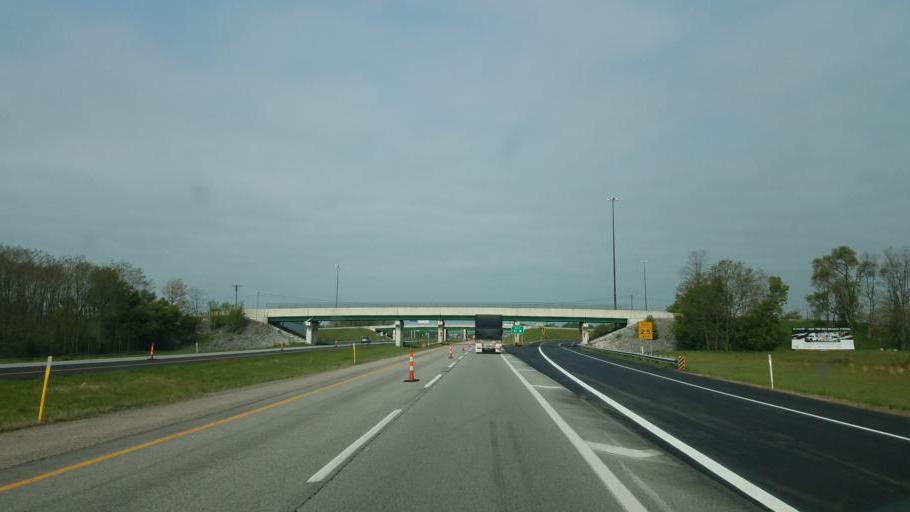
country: US
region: Indiana
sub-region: Elkhart County
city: Simonton Lake
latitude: 41.7311
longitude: -85.9646
